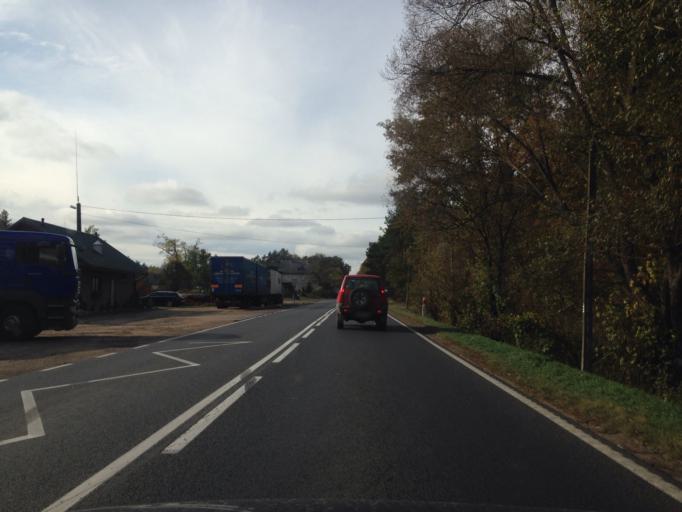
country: PL
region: Kujawsko-Pomorskie
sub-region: Powiat brodnicki
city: Brodnica
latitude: 53.2805
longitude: 19.4689
